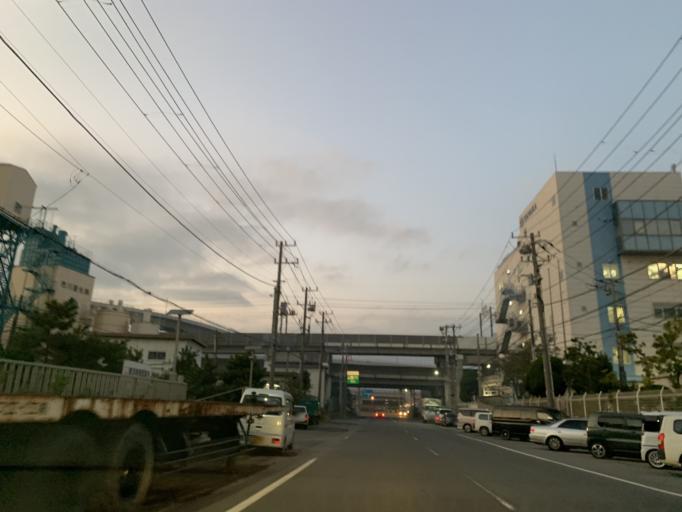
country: JP
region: Chiba
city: Funabashi
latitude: 35.6860
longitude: 139.9502
